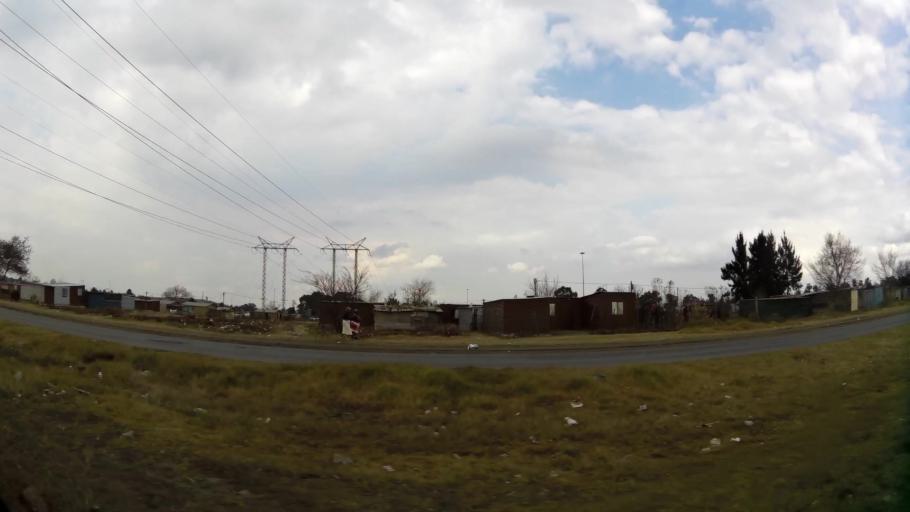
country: ZA
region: Gauteng
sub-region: Sedibeng District Municipality
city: Vanderbijlpark
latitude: -26.6675
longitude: 27.8388
